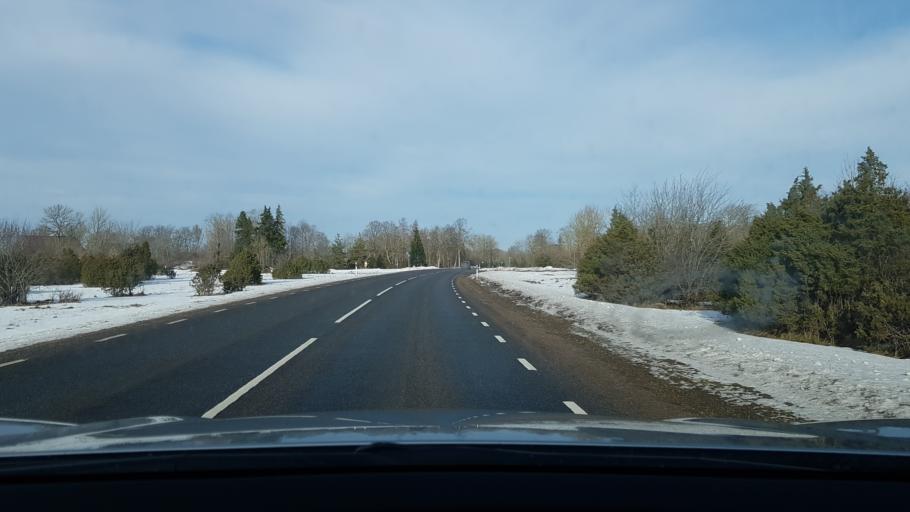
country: EE
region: Saare
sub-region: Kuressaare linn
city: Kuressaare
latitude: 58.2884
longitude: 22.5396
